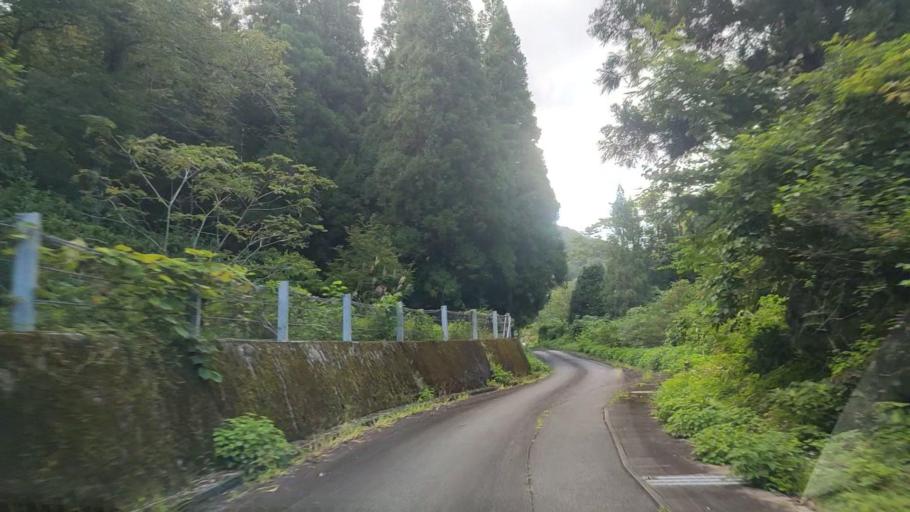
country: JP
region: Gifu
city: Takayama
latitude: 36.3133
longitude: 137.0863
